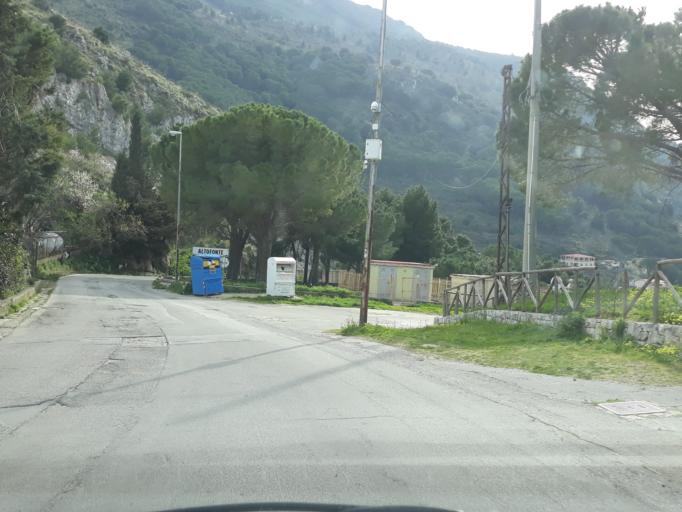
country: IT
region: Sicily
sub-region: Palermo
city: Altofonte
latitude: 38.0438
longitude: 13.3041
